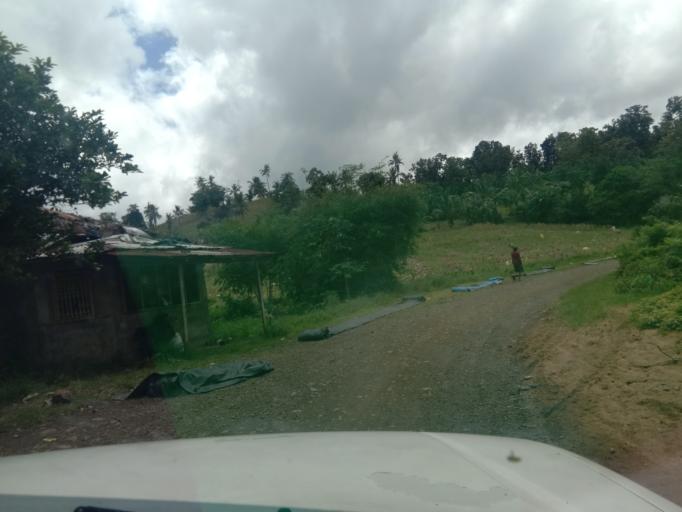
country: PH
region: Western Visayas
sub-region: Province of Capiz
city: Lantangan
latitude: 11.3578
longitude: 122.9101
